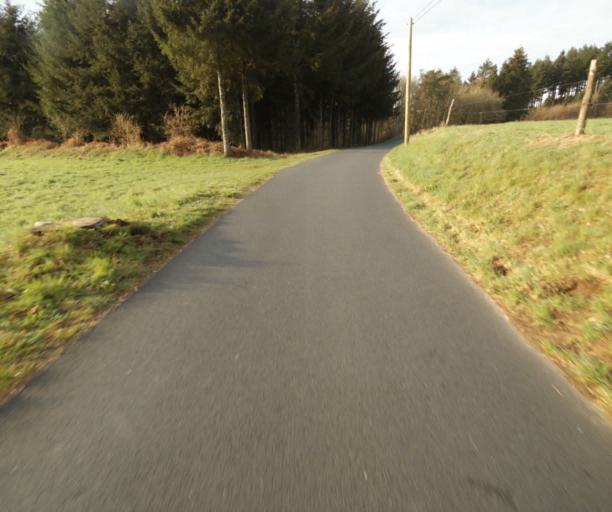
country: FR
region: Limousin
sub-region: Departement de la Correze
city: Correze
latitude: 45.4046
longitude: 1.8735
